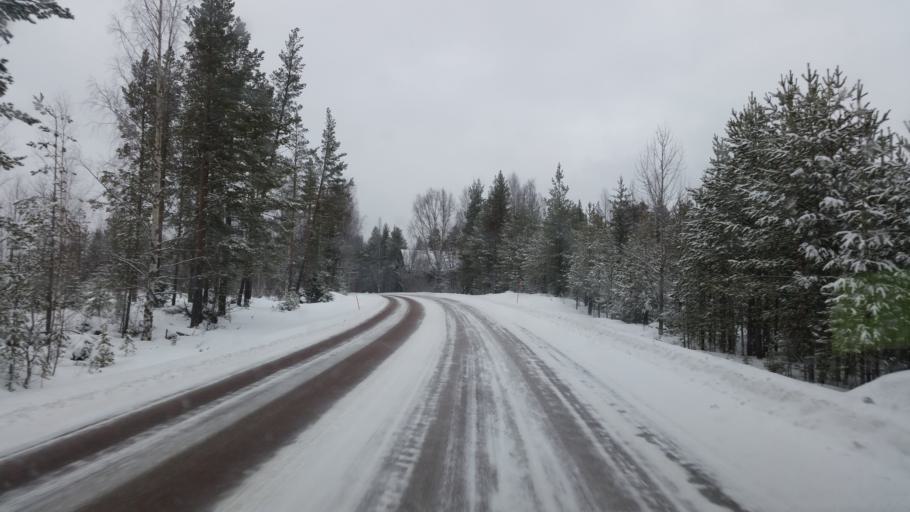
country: SE
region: Jaemtland
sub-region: Harjedalens Kommun
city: Sveg
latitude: 62.1933
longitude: 14.8612
